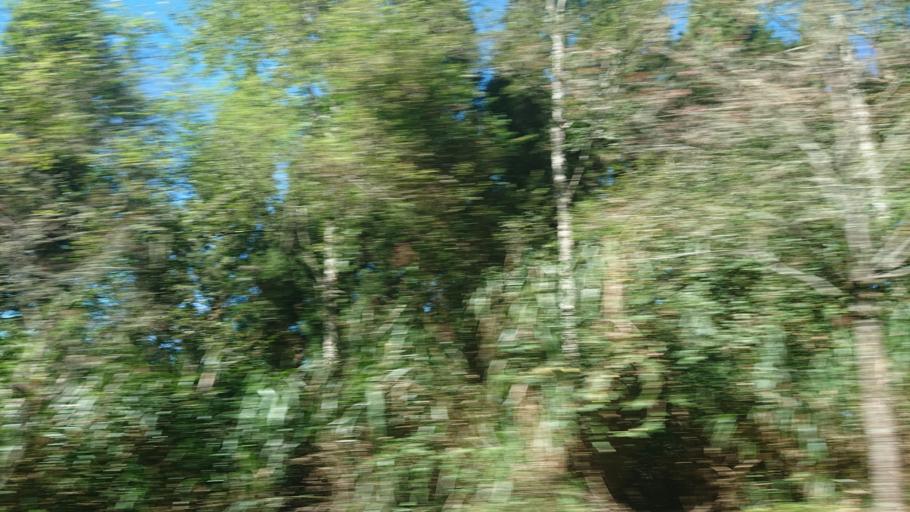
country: TW
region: Taiwan
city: Lugu
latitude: 23.4850
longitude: 120.8526
